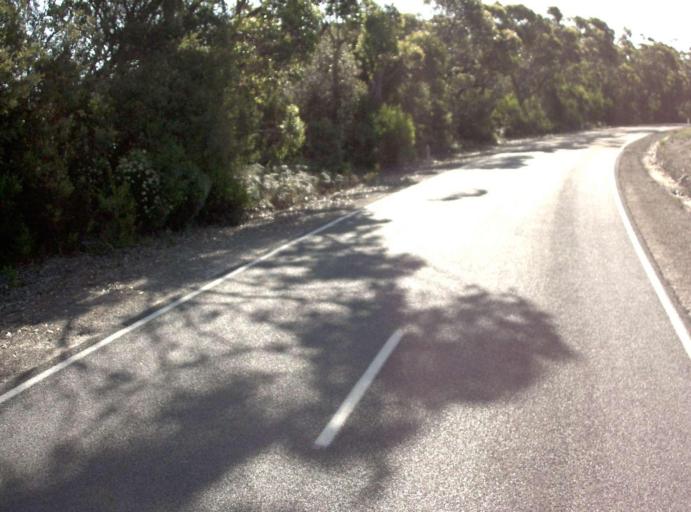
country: AU
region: Victoria
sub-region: East Gippsland
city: Lakes Entrance
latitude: -37.7980
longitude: 148.5588
